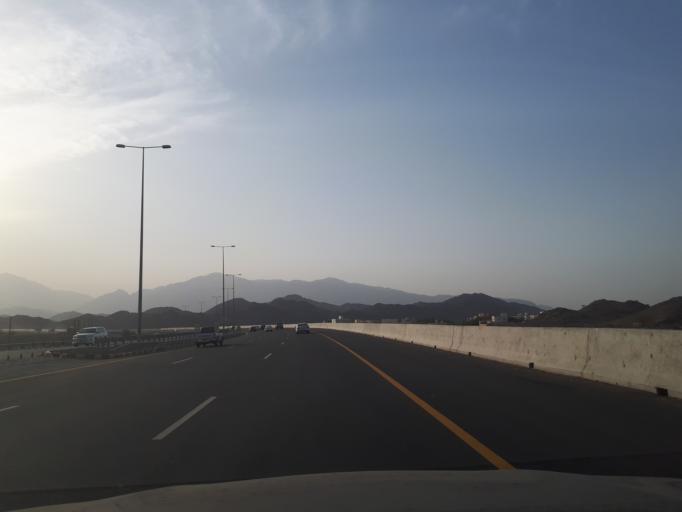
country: OM
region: Muhafazat ad Dakhiliyah
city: Bidbid
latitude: 23.3403
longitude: 58.1087
